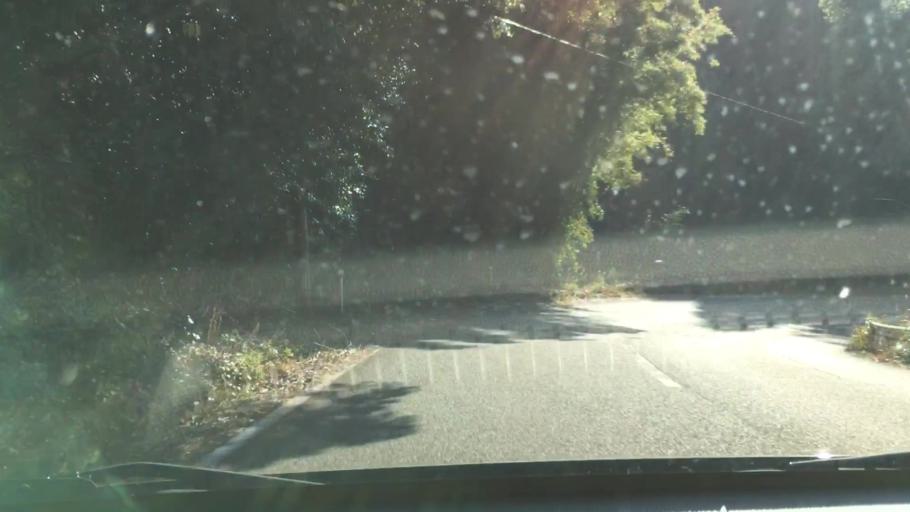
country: JP
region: Kagoshima
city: Kokubu-matsuki
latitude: 31.6693
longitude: 130.8312
